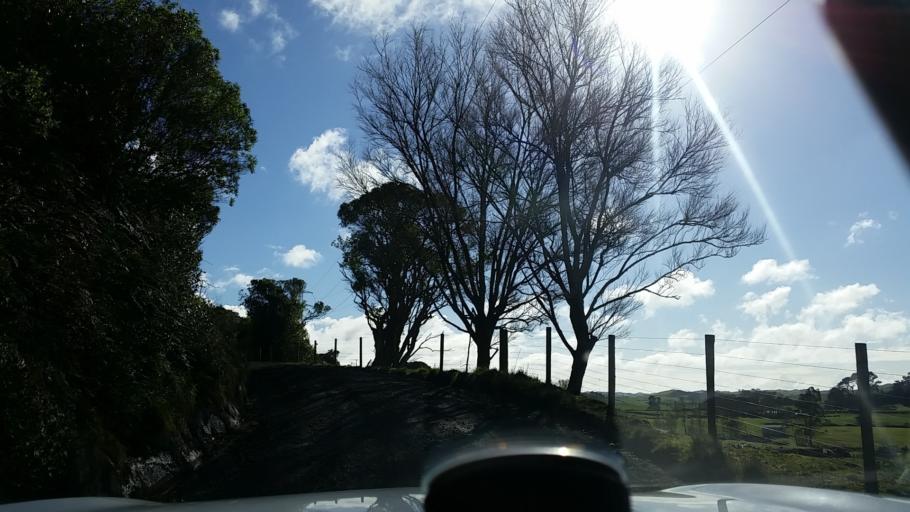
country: NZ
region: Taranaki
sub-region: South Taranaki District
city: Eltham
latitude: -39.4560
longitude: 174.3691
